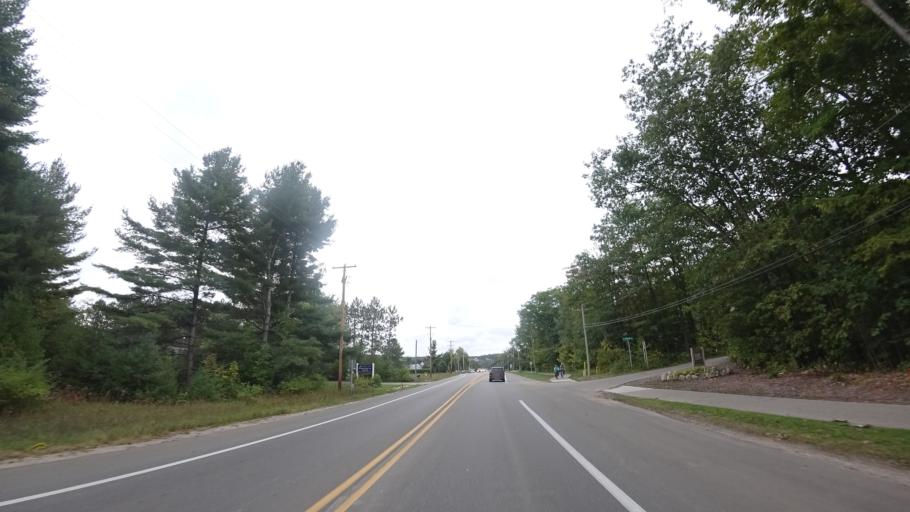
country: US
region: Michigan
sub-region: Emmet County
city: Petoskey
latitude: 45.4066
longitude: -84.9021
